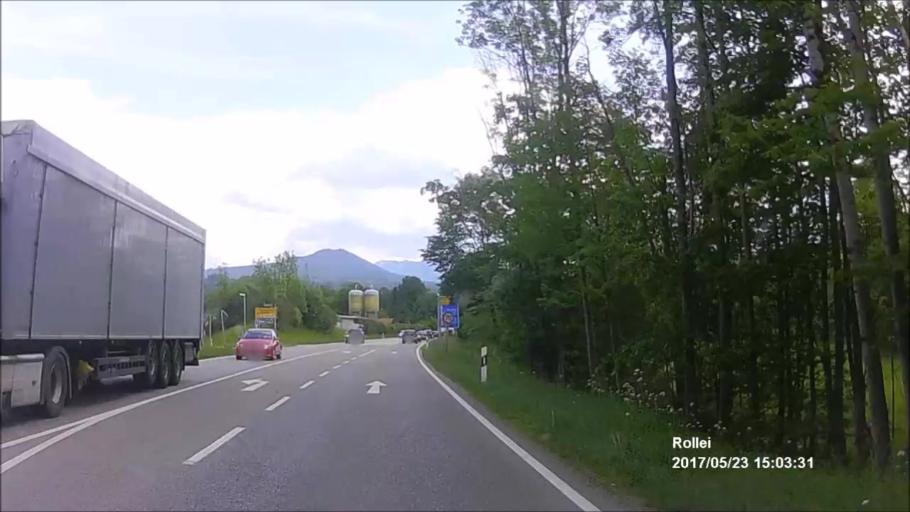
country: DE
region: Bavaria
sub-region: Upper Bavaria
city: Siegsdorf
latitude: 47.8319
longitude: 12.6478
